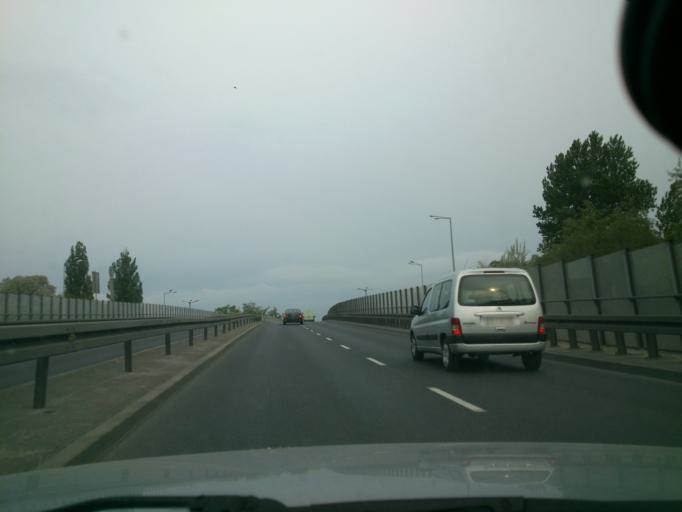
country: PL
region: Lesser Poland Voivodeship
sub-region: Krakow
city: Krakow
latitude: 50.0864
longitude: 19.9525
